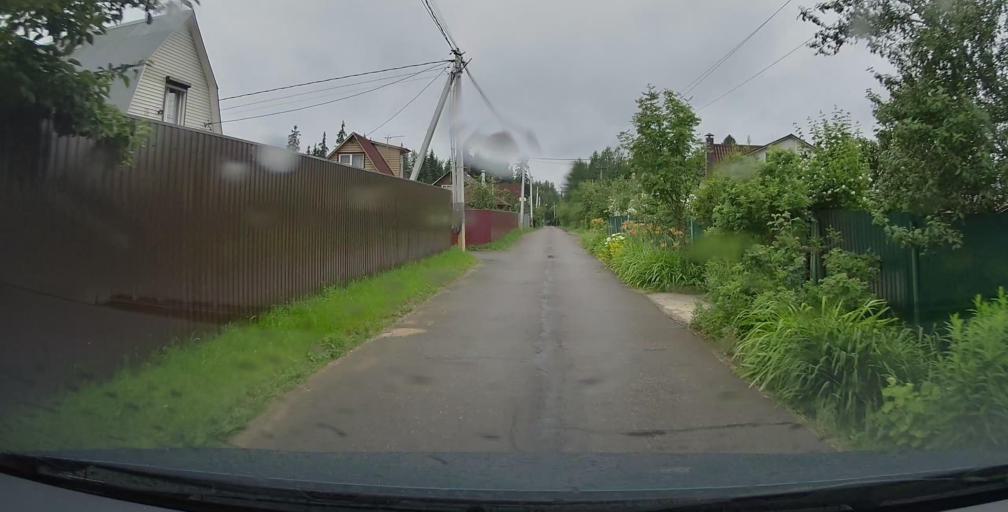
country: RU
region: Moskovskaya
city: Selyatino
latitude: 55.3950
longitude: 37.0119
